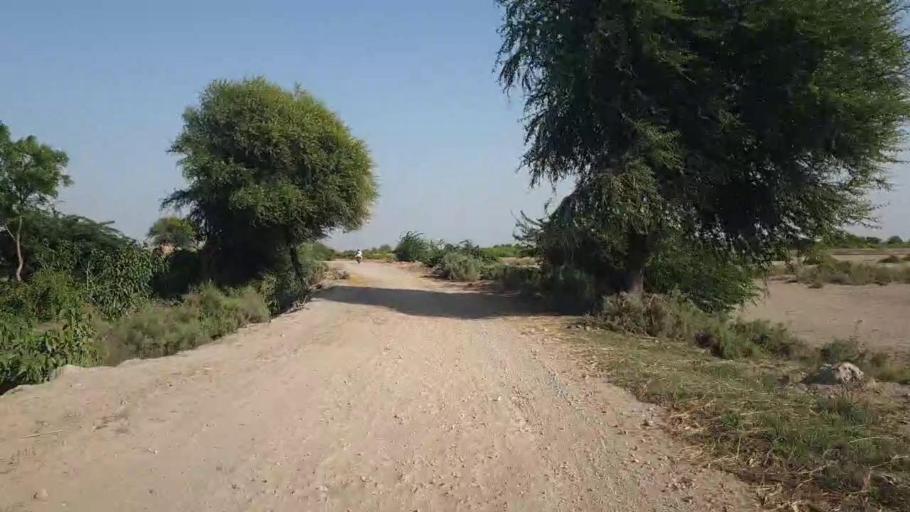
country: PK
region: Sindh
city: Rajo Khanani
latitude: 25.0093
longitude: 68.7847
